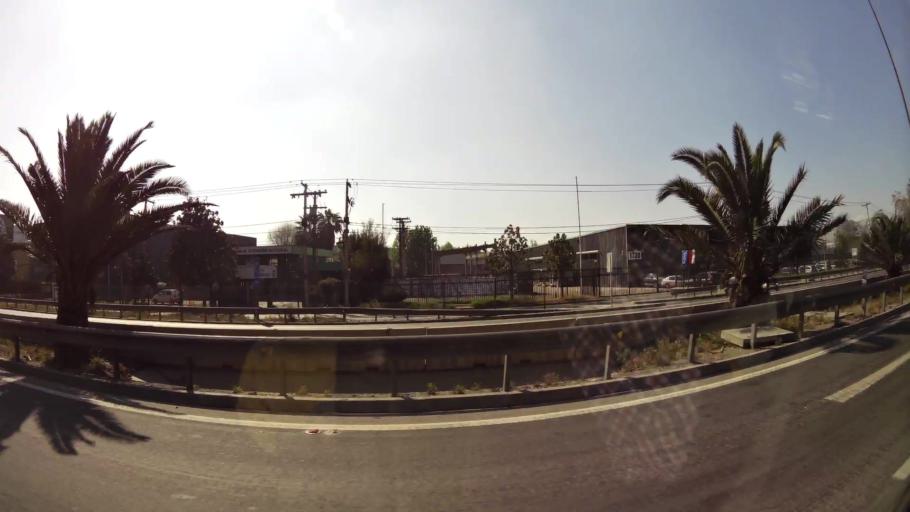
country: CL
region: Santiago Metropolitan
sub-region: Provincia de Santiago
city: Lo Prado
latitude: -33.3738
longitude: -70.7125
